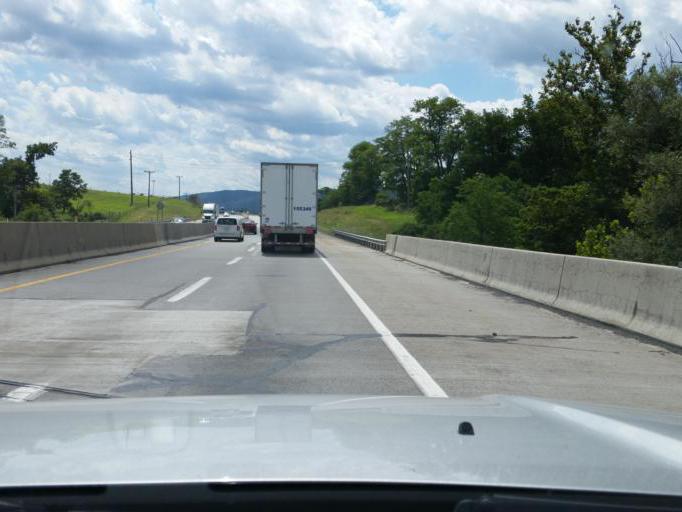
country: US
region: Pennsylvania
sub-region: Franklin County
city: Doylestown
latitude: 40.1198
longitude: -77.7767
